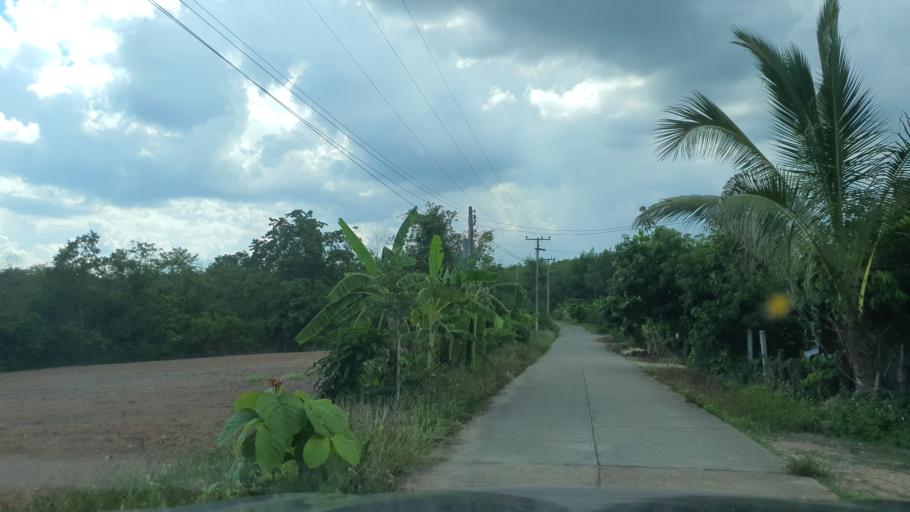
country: TH
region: Chiang Mai
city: Mae Taeng
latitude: 19.1165
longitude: 99.0620
